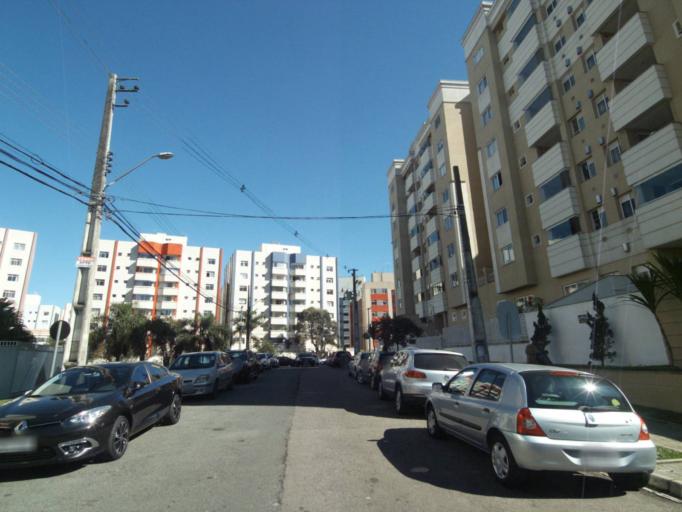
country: BR
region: Parana
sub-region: Curitiba
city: Curitiba
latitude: -25.4008
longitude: -49.2566
